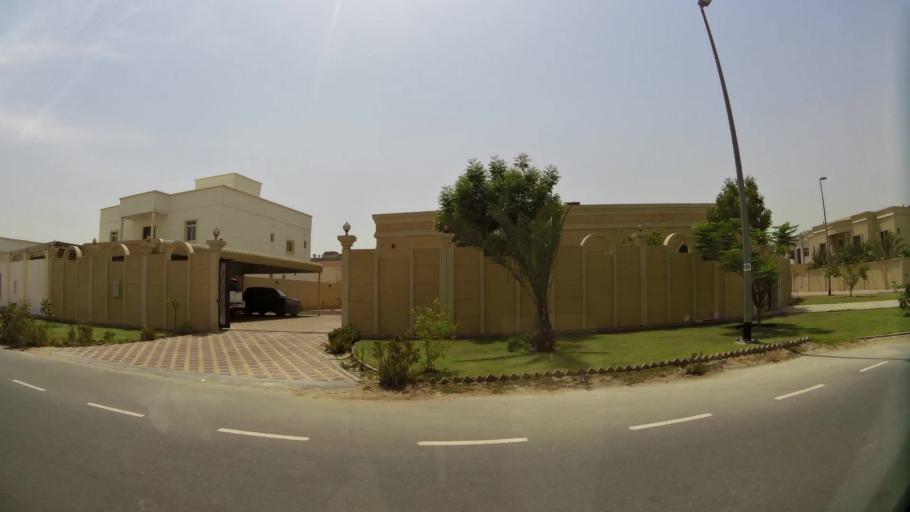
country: AE
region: Ash Shariqah
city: Sharjah
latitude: 25.2602
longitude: 55.4866
